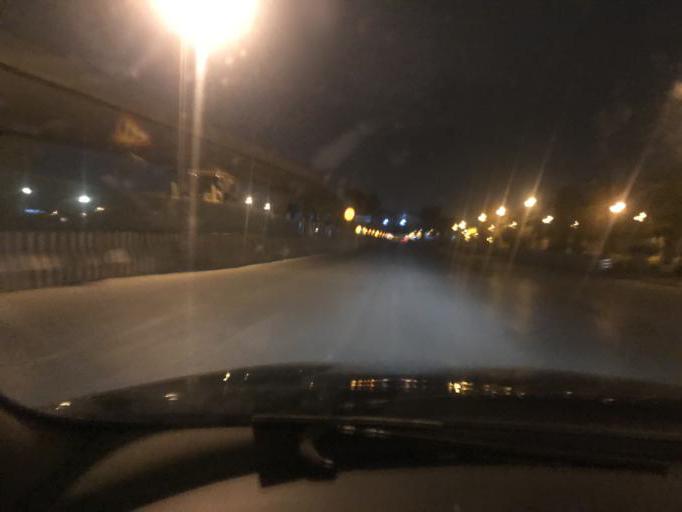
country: SA
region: Ar Riyad
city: Riyadh
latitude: 24.8029
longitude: 46.6990
